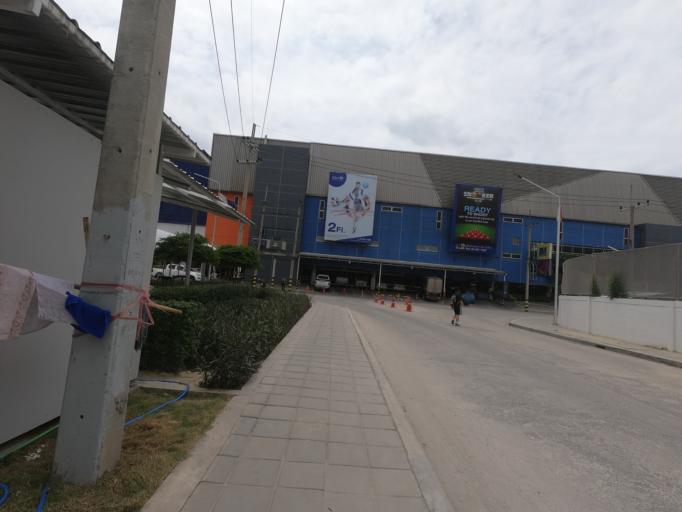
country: TH
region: Bangkok
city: Sai Mai
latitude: 13.9382
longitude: 100.6524
